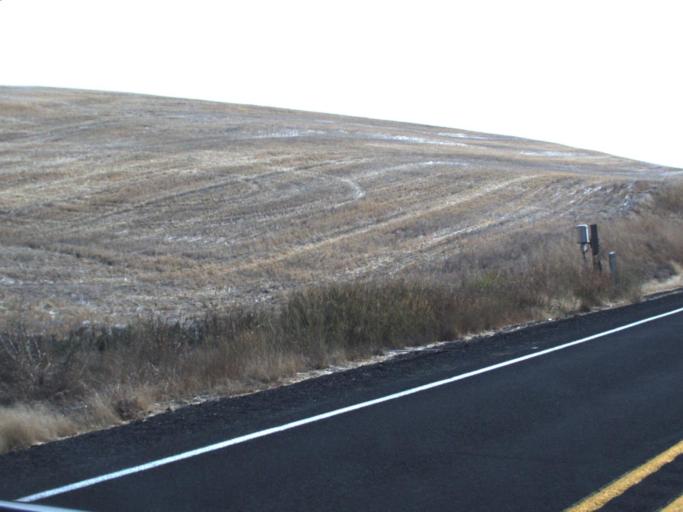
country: US
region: Washington
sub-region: Whitman County
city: Pullman
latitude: 46.9694
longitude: -117.1183
